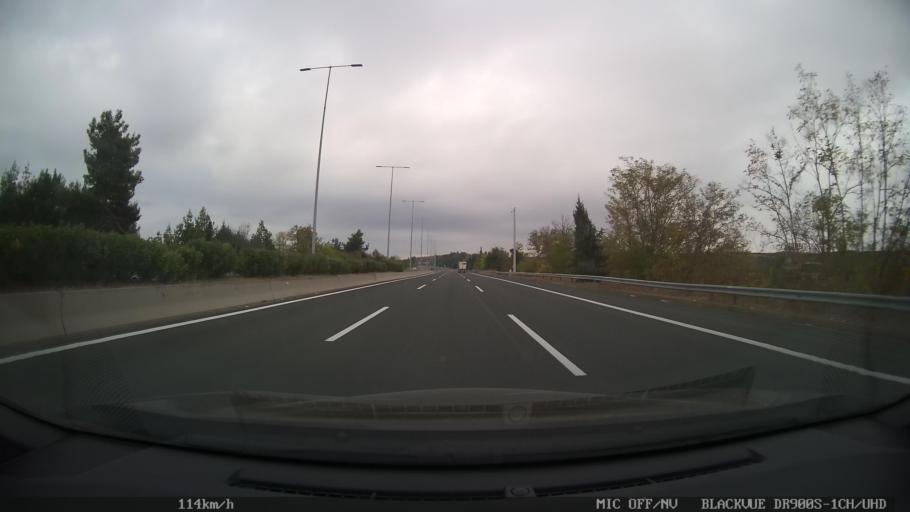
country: GR
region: Central Macedonia
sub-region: Nomos Pierias
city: Makrygialos
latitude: 40.4192
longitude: 22.5905
